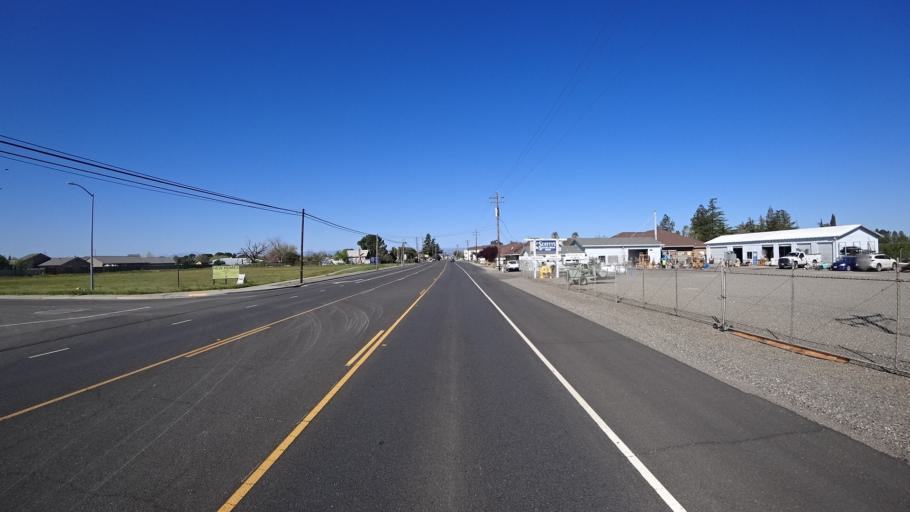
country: US
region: California
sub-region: Glenn County
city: Orland
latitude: 39.7472
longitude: -122.1709
